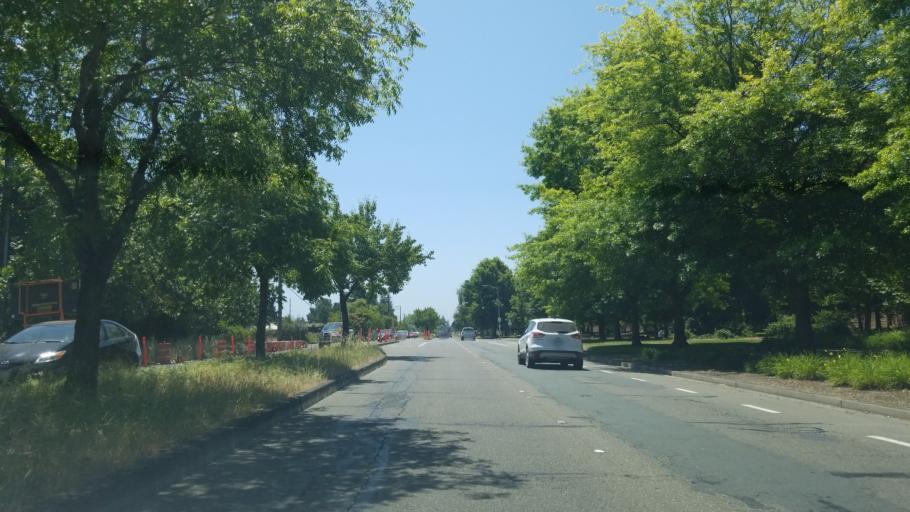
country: US
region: California
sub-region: Sonoma County
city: Roseland
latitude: 38.4323
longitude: -122.7698
